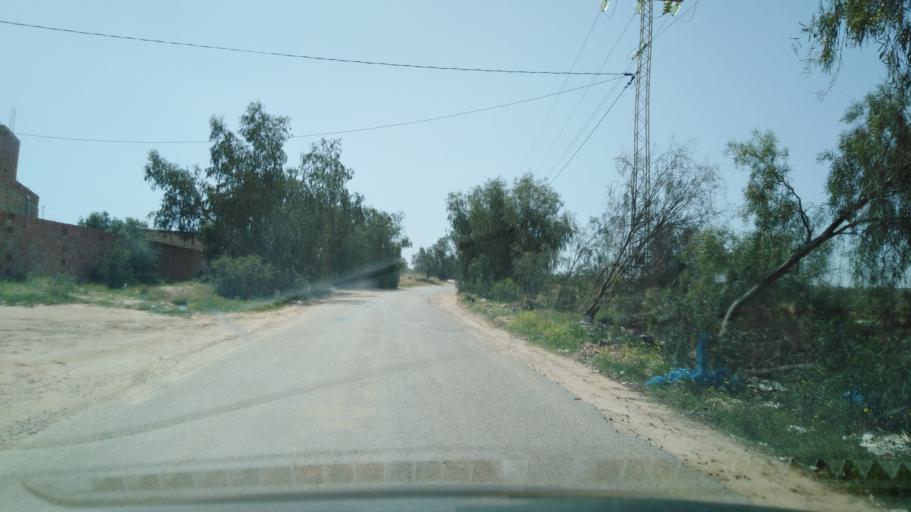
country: TN
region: Safaqis
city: Sfax
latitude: 34.7228
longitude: 10.5303
